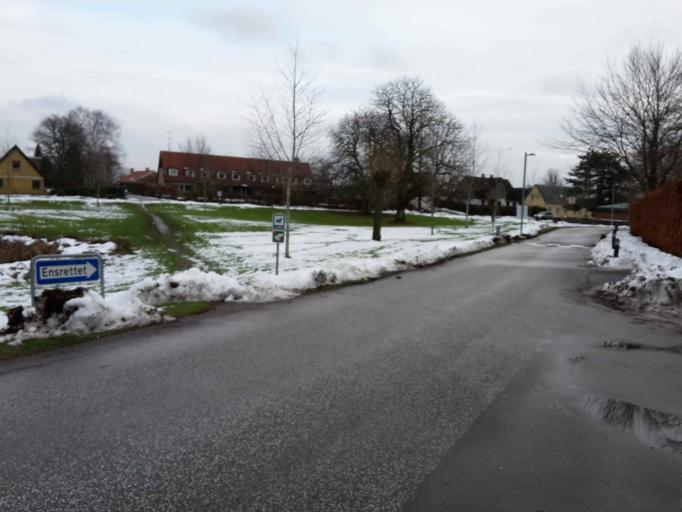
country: DK
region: Capital Region
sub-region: Allerod Kommune
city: Blovstrod
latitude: 55.8663
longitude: 12.3871
